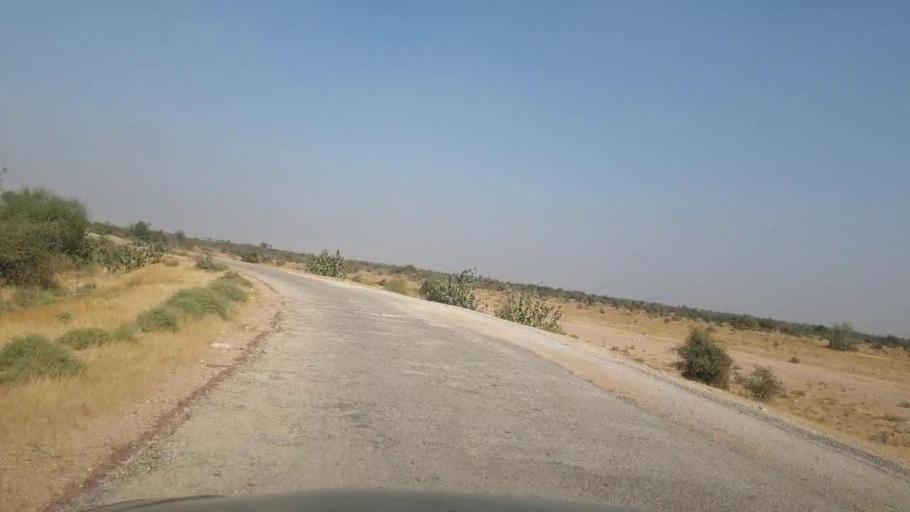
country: PK
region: Sindh
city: Jamshoro
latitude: 25.4732
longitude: 67.8205
